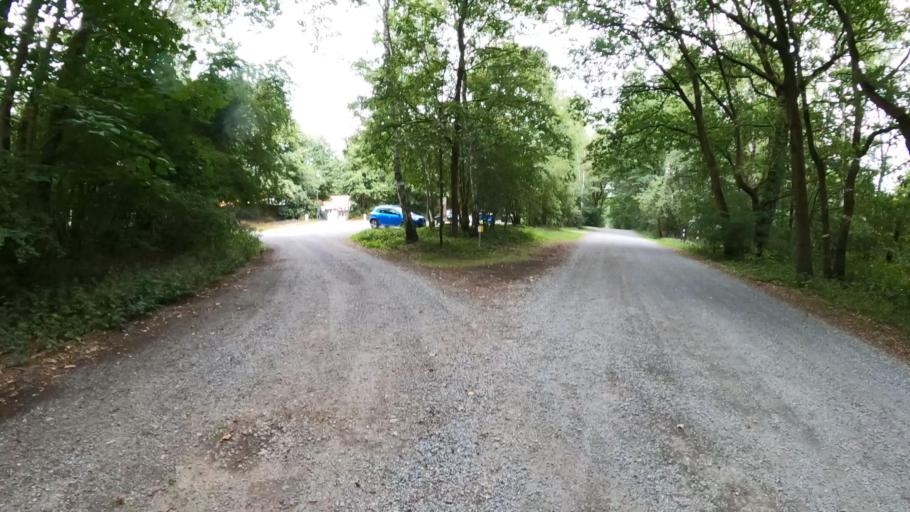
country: DE
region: Lower Saxony
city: Buchholz in der Nordheide
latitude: 53.3361
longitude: 9.8988
